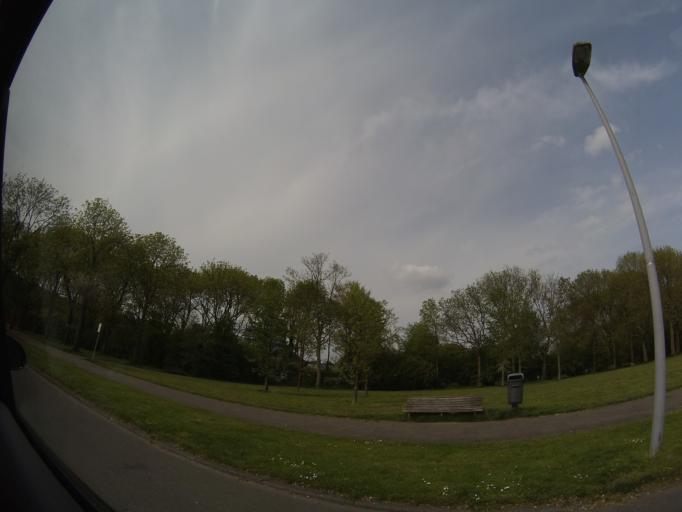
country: NL
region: North Holland
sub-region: Gemeente Ouder-Amstel
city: Duivendrecht
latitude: 52.3376
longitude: 4.9031
